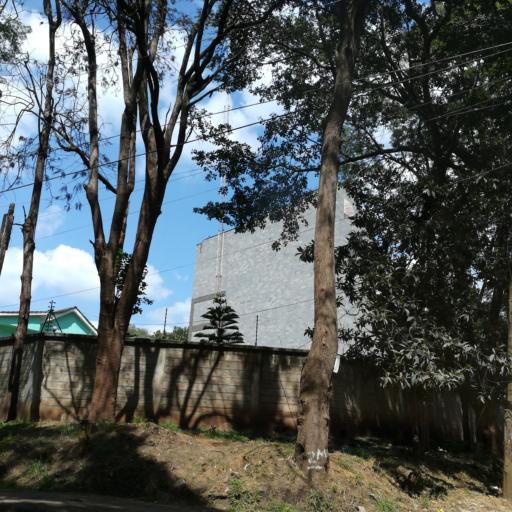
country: KE
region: Nairobi Area
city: Nairobi
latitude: -1.2962
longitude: 36.7928
